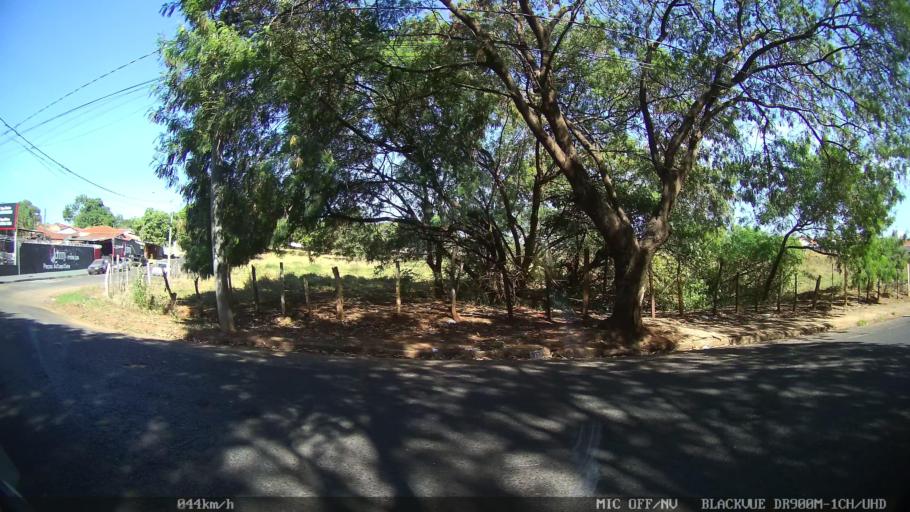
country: BR
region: Sao Paulo
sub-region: Sao Jose Do Rio Preto
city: Sao Jose do Rio Preto
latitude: -20.7776
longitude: -49.3952
